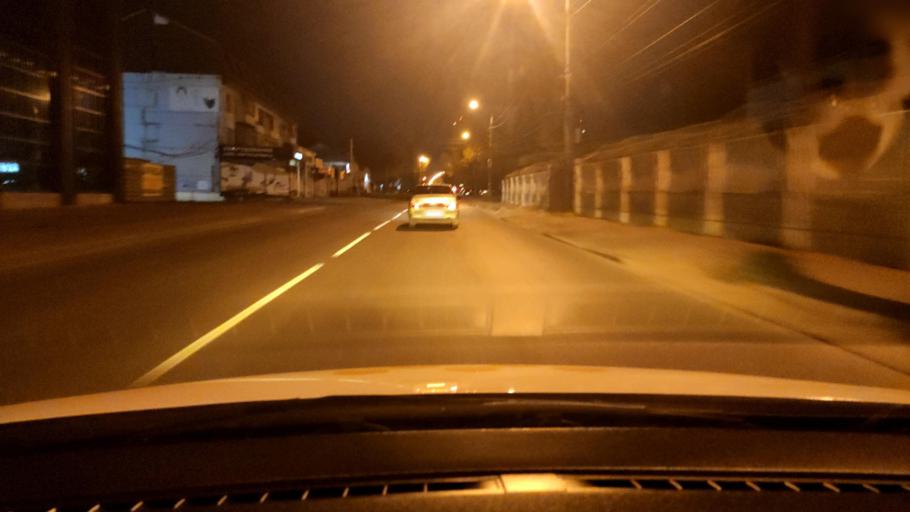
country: RU
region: Voronezj
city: Voronezh
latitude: 51.6643
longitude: 39.1468
